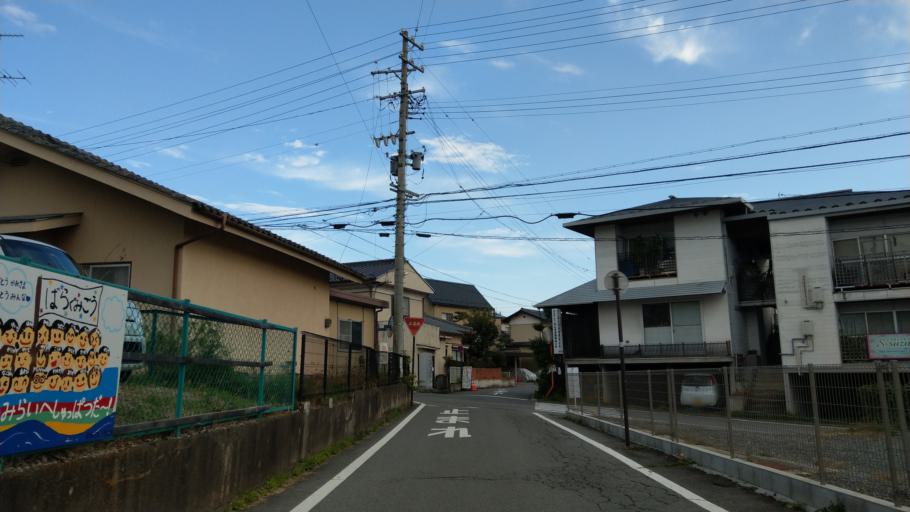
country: JP
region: Nagano
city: Komoro
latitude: 36.3316
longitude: 138.4231
